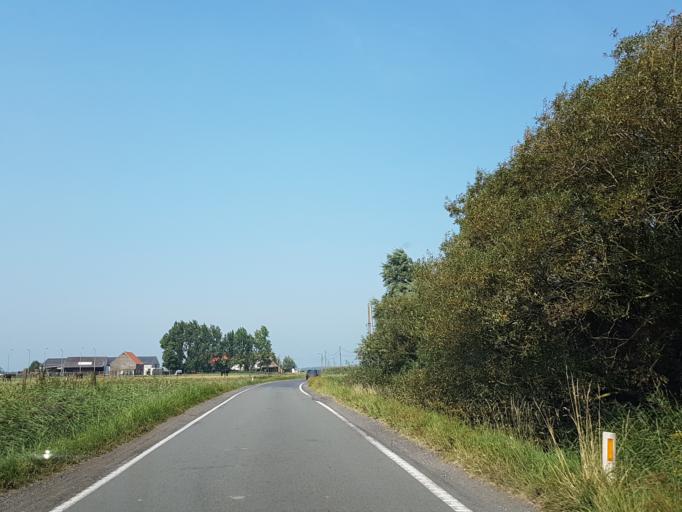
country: BE
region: Flanders
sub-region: Provincie West-Vlaanderen
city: De Haan
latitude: 51.2341
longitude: 3.0603
